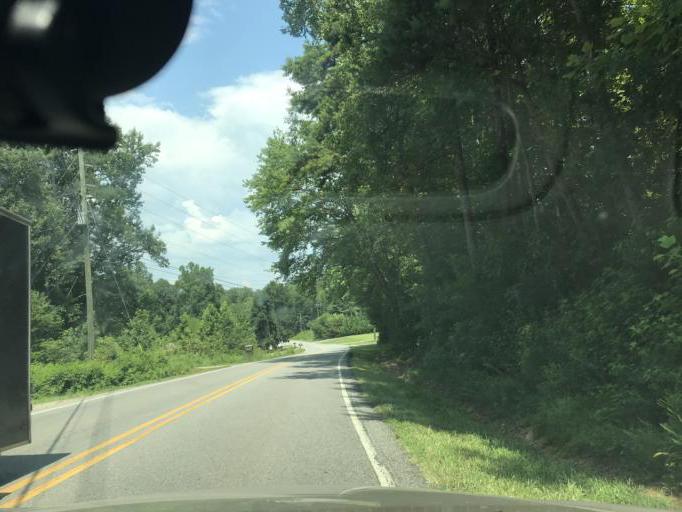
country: US
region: Georgia
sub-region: Forsyth County
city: Cumming
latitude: 34.3013
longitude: -84.1557
